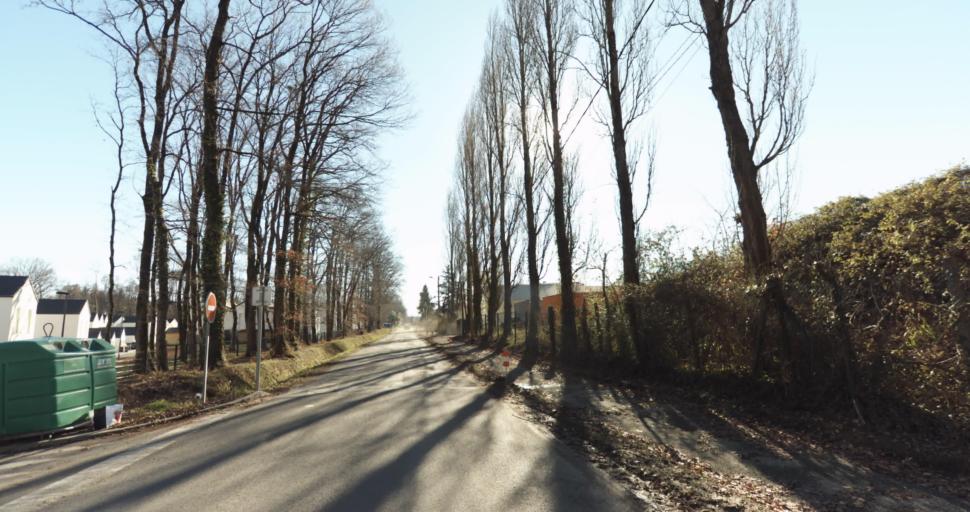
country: FR
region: Aquitaine
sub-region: Departement des Pyrenees-Atlantiques
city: Buros
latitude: 43.3301
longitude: -0.2997
